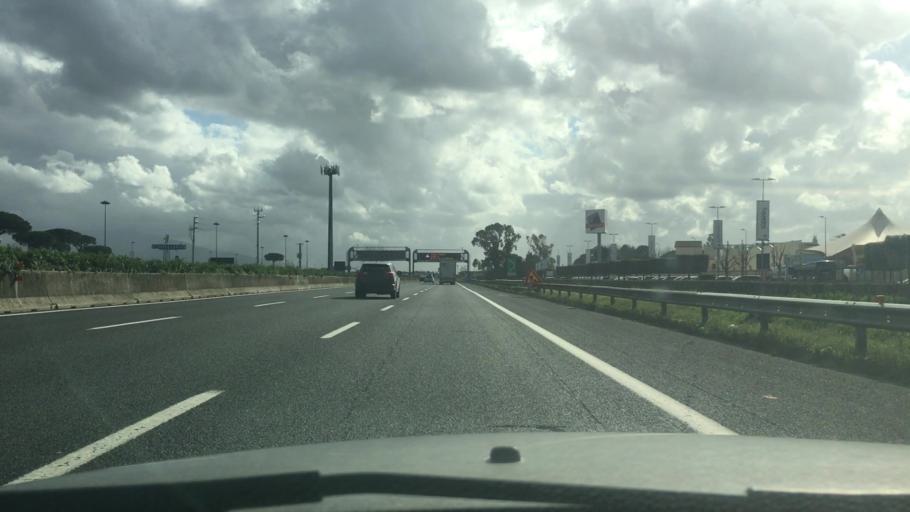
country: IT
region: Campania
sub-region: Provincia di Caserta
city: Marcianise
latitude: 41.0086
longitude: 14.3230
